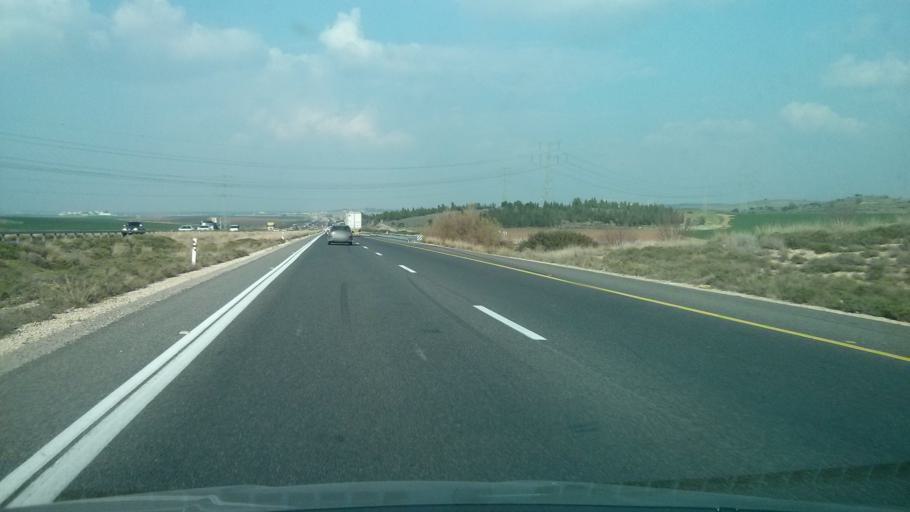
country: IL
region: Southern District
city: Qiryat Gat
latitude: 31.6828
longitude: 34.8085
